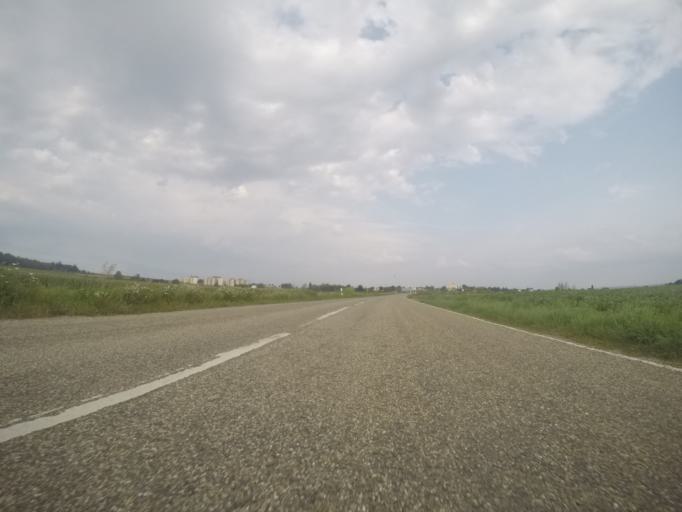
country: DE
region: Baden-Wuerttemberg
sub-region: Regierungsbezirk Stuttgart
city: Hemmingen
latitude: 48.8656
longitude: 9.0137
